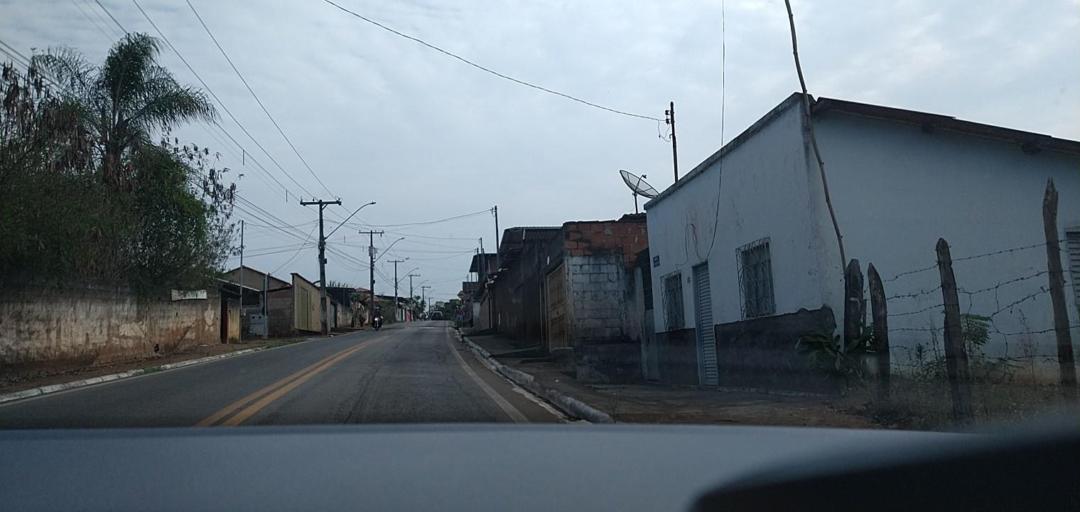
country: BR
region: Minas Gerais
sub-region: Rio Piracicaba
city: Rio Piracicaba
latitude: -19.8957
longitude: -43.1437
